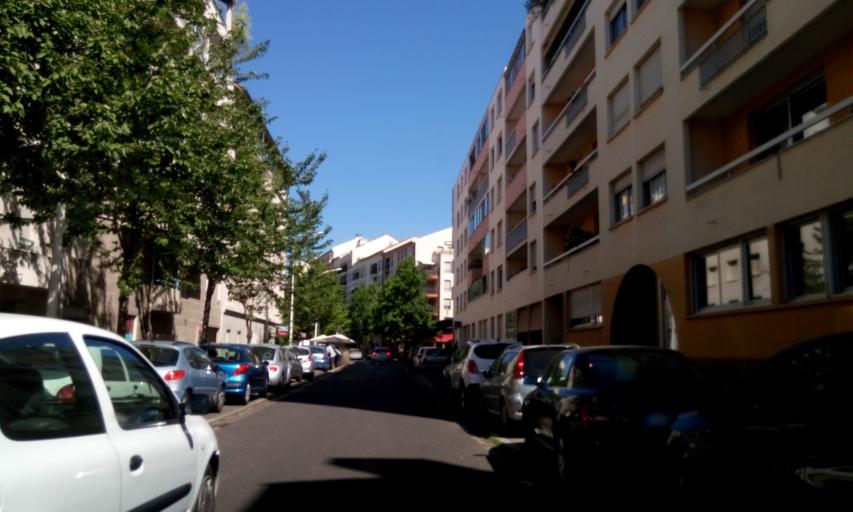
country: FR
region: Rhone-Alpes
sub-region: Departement du Rhone
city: Lyon
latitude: 45.7562
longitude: 4.8641
